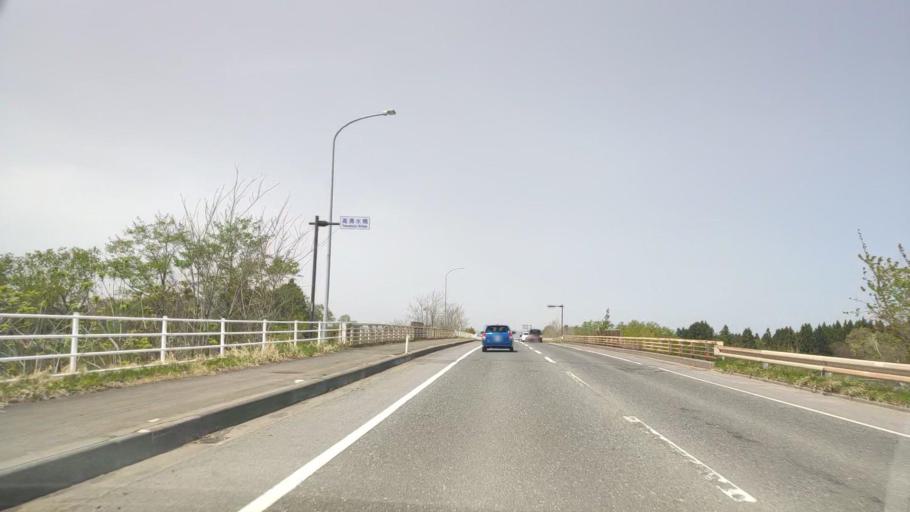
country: JP
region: Aomori
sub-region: Misawa Shi
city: Inuotose
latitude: 40.6308
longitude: 141.2483
